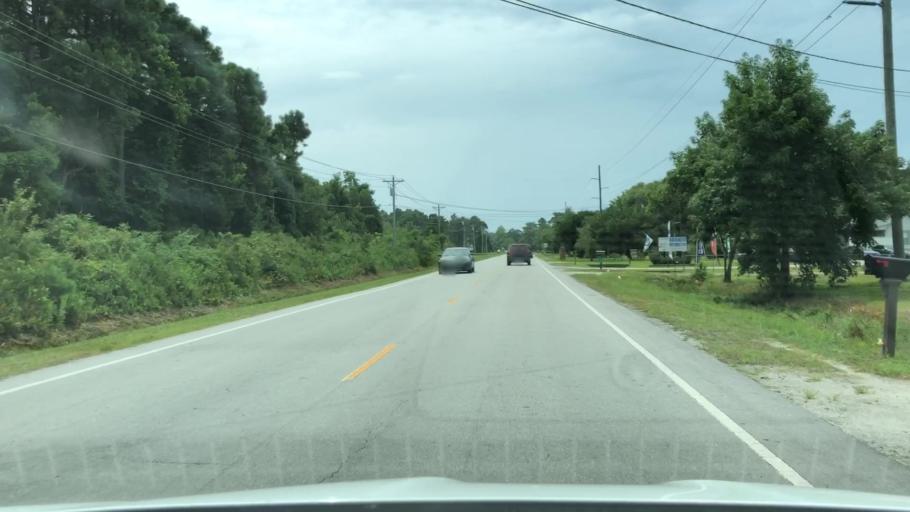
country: US
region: North Carolina
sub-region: Carteret County
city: Broad Creek
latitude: 34.7369
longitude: -76.8868
